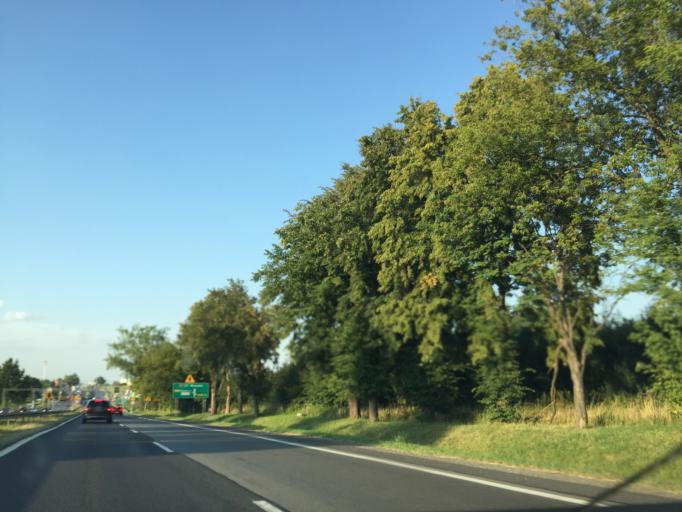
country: PL
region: Masovian Voivodeship
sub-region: Powiat piaseczynski
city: Tarczyn
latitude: 51.9751
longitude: 20.8364
